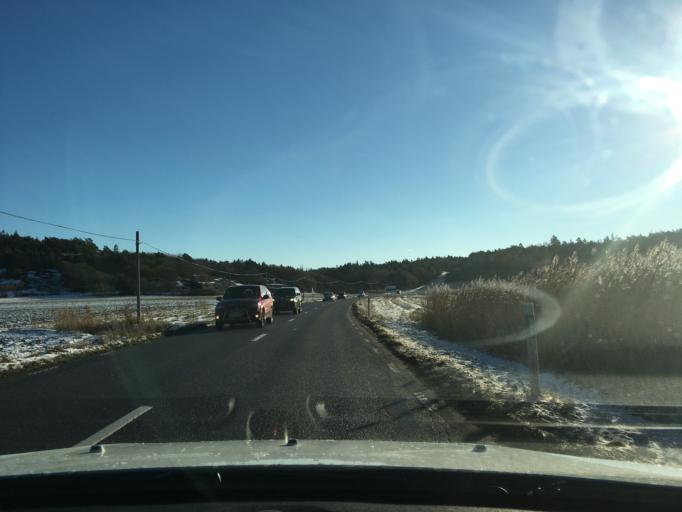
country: SE
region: Vaestra Goetaland
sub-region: Tjorns Kommun
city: Myggenas
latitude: 58.1035
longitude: 11.7058
